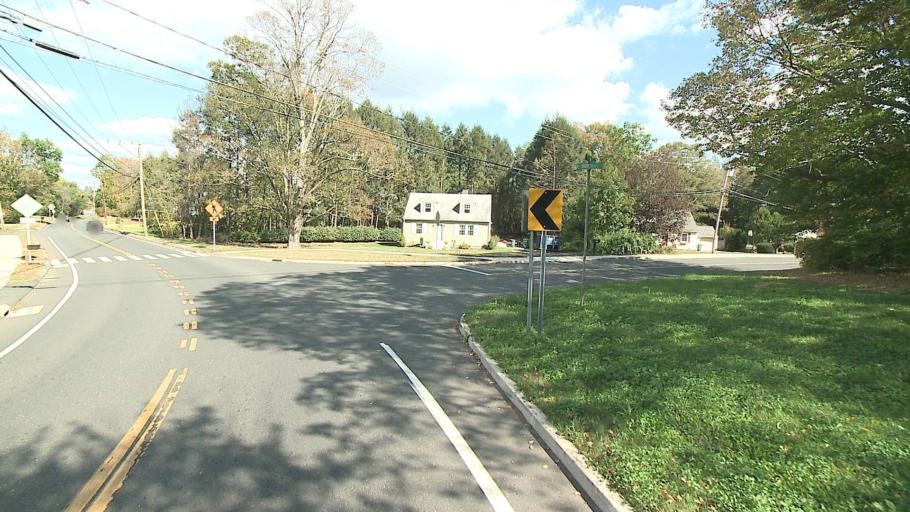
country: US
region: Connecticut
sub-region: New Haven County
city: Cheshire
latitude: 41.4773
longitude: -72.9099
